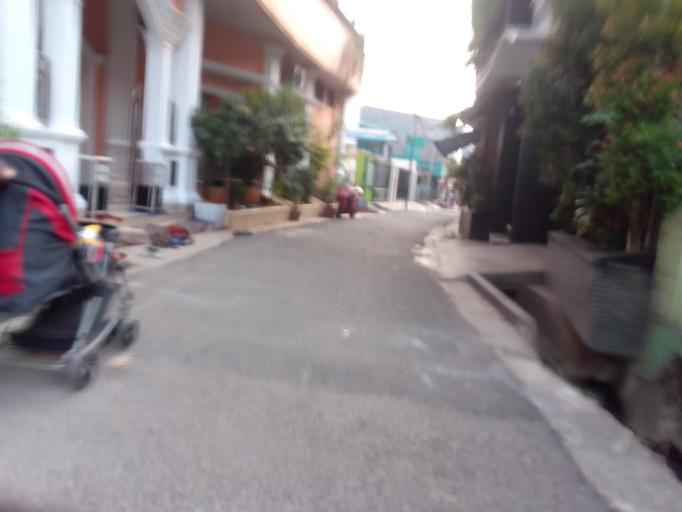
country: ID
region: Jakarta Raya
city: Jakarta
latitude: -6.1937
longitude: 106.8128
